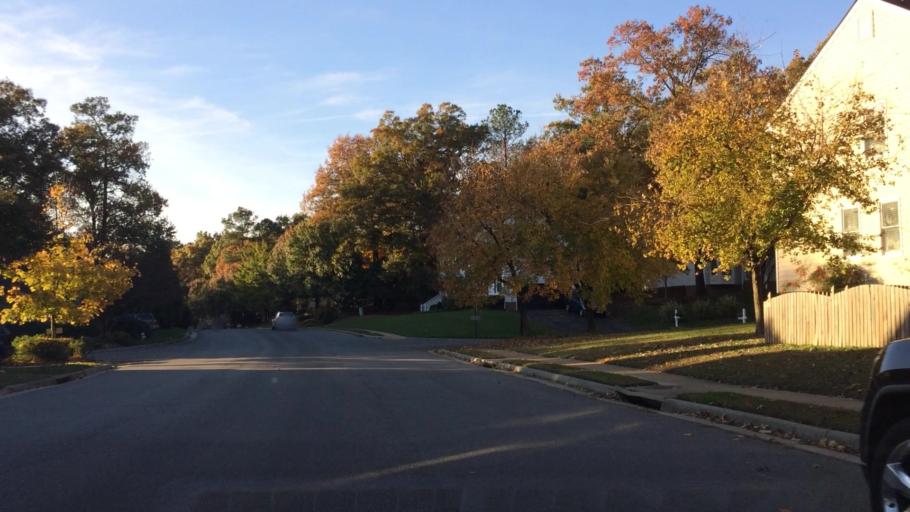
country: US
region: Virginia
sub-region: Henrico County
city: Chamberlayne
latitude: 37.6876
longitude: -77.4199
